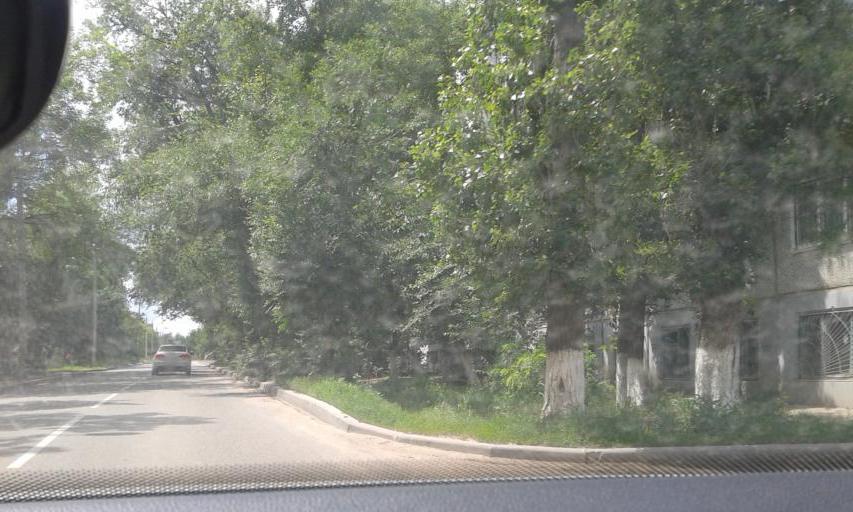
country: RU
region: Volgograd
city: Gorodishche
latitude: 48.7724
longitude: 44.4884
